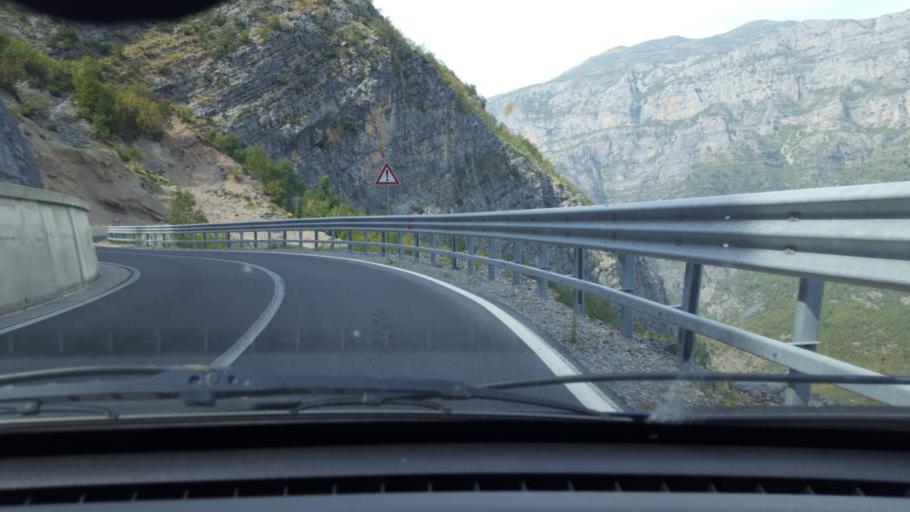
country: AL
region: Shkoder
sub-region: Rrethi i Malesia e Madhe
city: Kastrat
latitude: 42.4160
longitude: 19.4976
